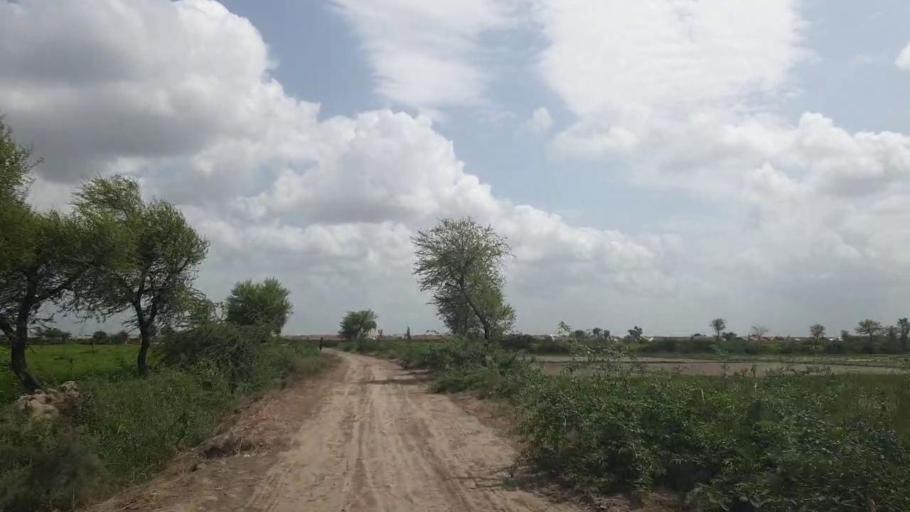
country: PK
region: Sindh
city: Tando Bago
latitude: 24.6522
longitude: 68.9981
